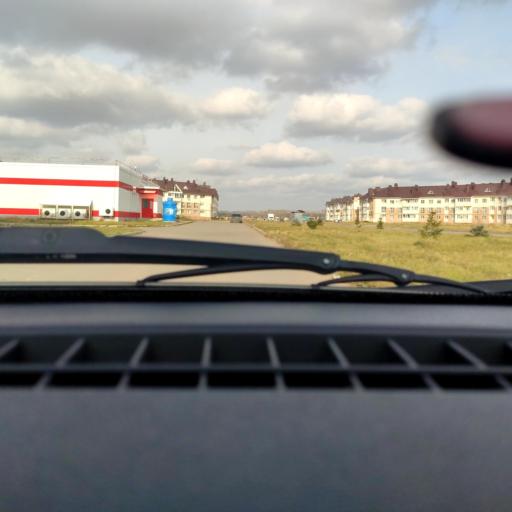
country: RU
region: Bashkortostan
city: Ufa
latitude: 54.8330
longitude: 56.1684
